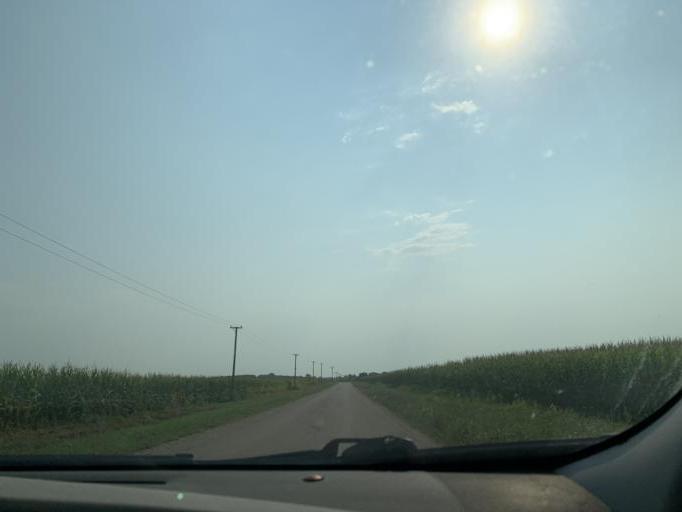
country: US
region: Illinois
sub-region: Whiteside County
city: Morrison
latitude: 41.8697
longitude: -89.8993
